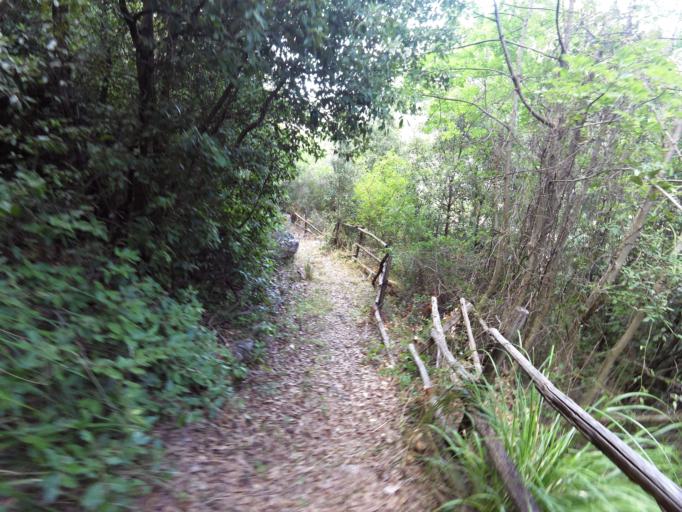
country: IT
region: Calabria
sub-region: Provincia di Reggio Calabria
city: Pazzano
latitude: 38.4731
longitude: 16.4515
